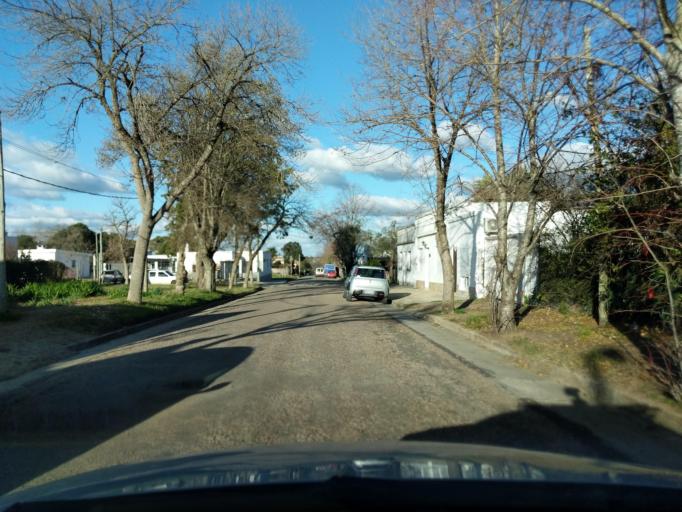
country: UY
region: Florida
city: Florida
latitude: -34.0990
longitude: -56.2306
